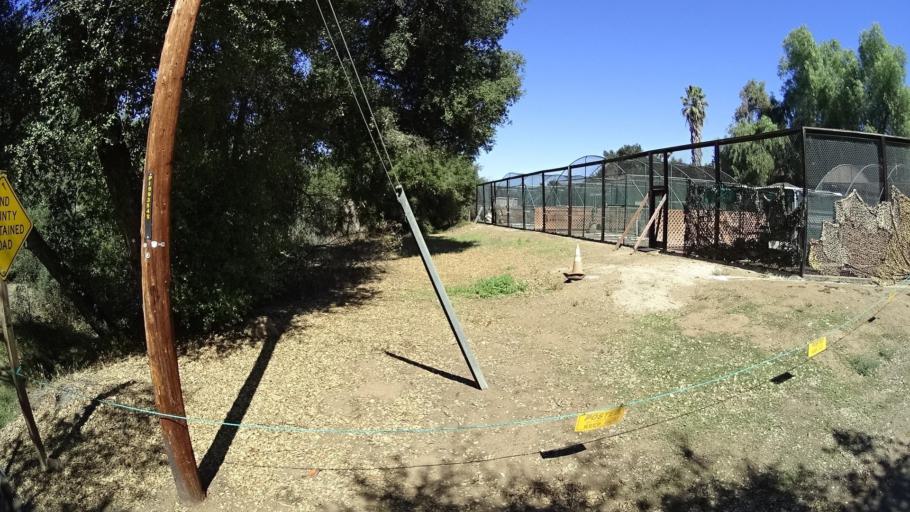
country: US
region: California
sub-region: San Diego County
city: Alpine
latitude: 32.7751
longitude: -116.7282
